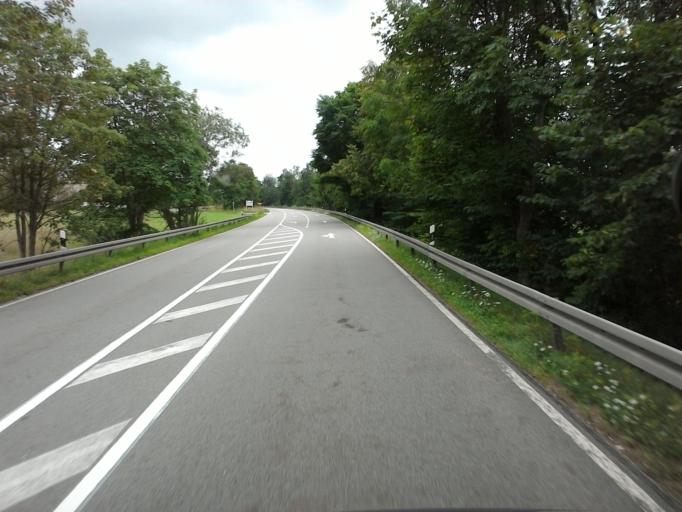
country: DE
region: Bavaria
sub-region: Upper Bavaria
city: Weyarn
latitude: 47.8306
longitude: 11.8227
